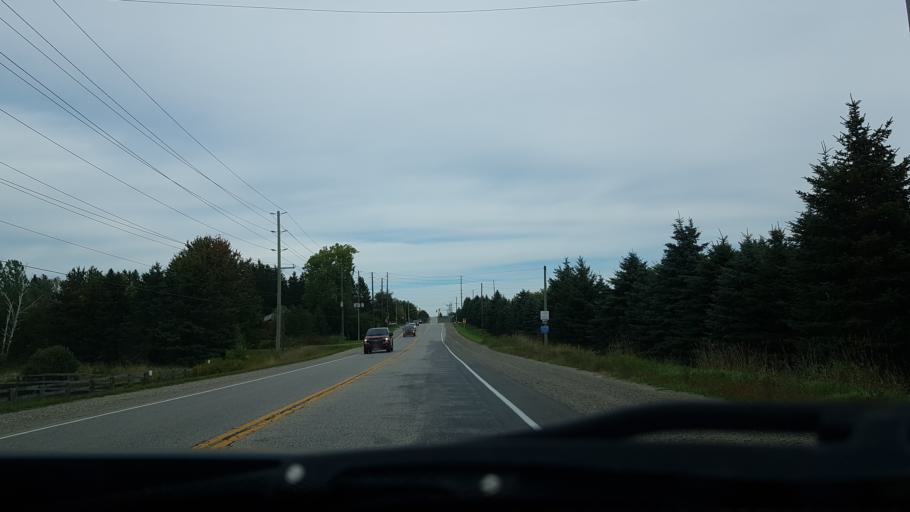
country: CA
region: Ontario
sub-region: Wellington County
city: Guelph
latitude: 43.6461
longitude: -80.1888
